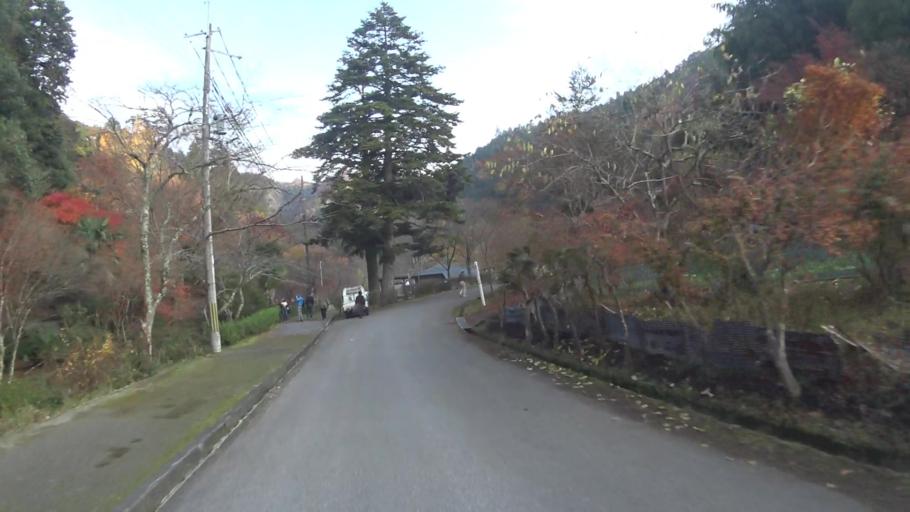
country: JP
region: Kyoto
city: Maizuru
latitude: 35.4760
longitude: 135.4470
